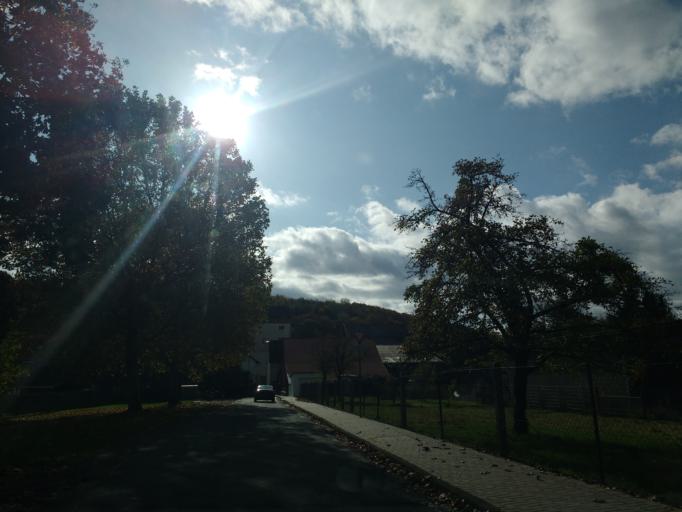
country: DE
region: Lower Saxony
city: Herzberg am Harz
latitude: 51.6290
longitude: 10.3844
